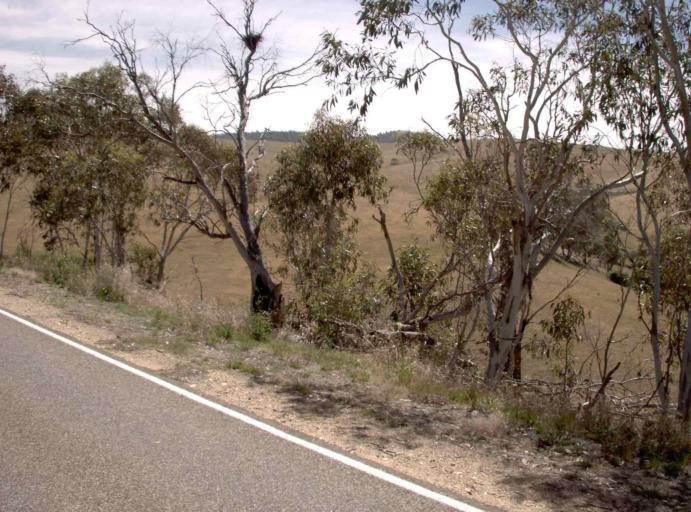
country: AU
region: Victoria
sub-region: Alpine
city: Mount Beauty
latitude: -37.0638
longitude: 147.6147
